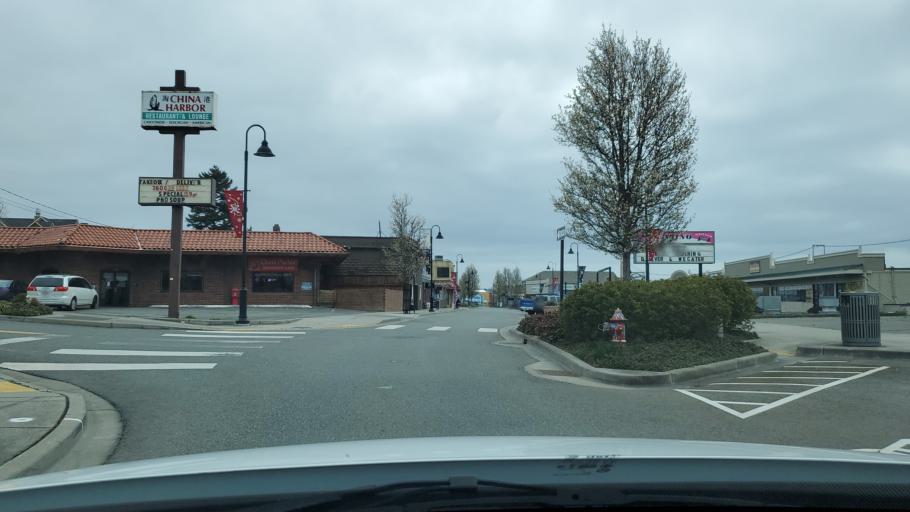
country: US
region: Washington
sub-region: Island County
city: Oak Harbor
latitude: 48.2882
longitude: -122.6508
